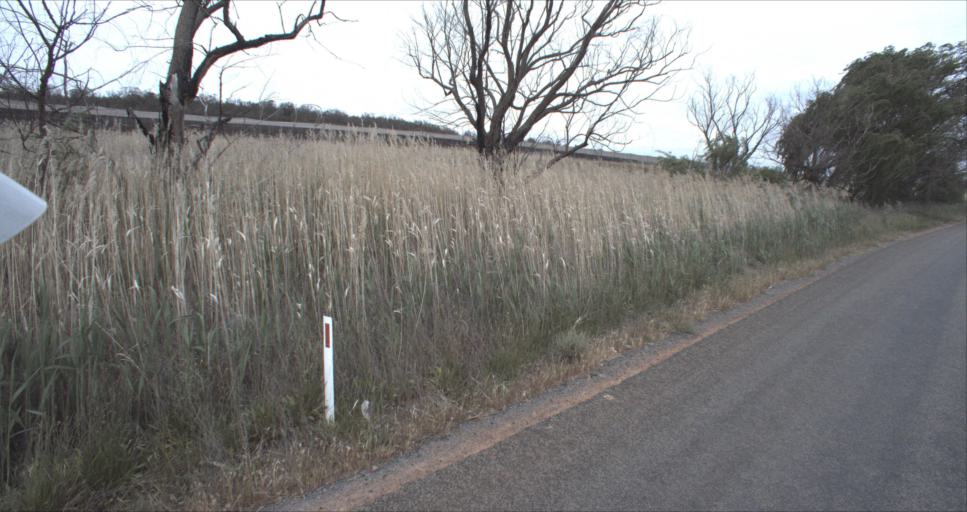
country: AU
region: New South Wales
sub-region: Leeton
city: Leeton
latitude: -34.4290
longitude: 146.3779
